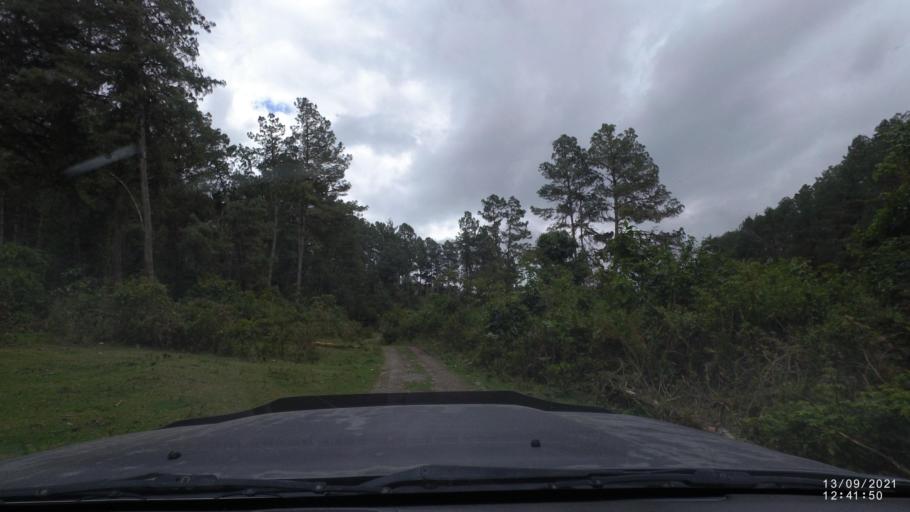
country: BO
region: Cochabamba
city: Colomi
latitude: -17.2557
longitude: -65.8171
